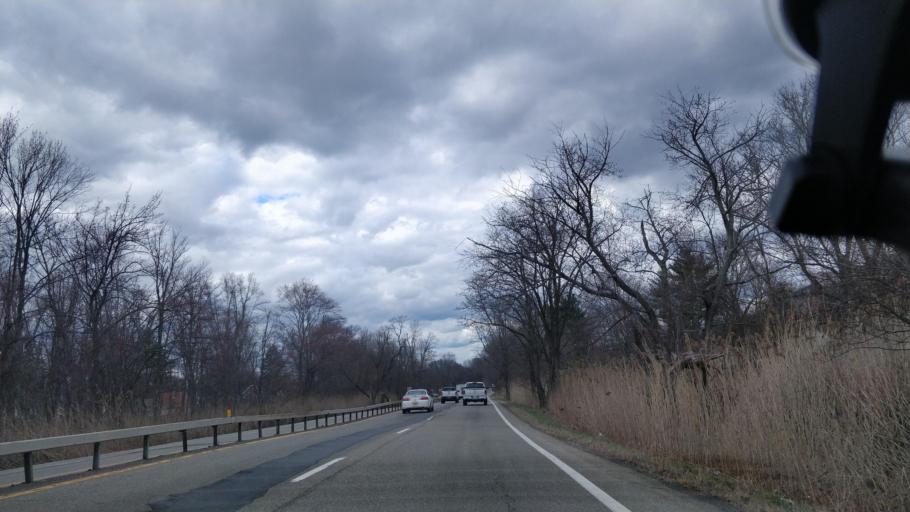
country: US
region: New York
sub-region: Westchester County
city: Briarcliff Manor
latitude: 41.1639
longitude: -73.8378
